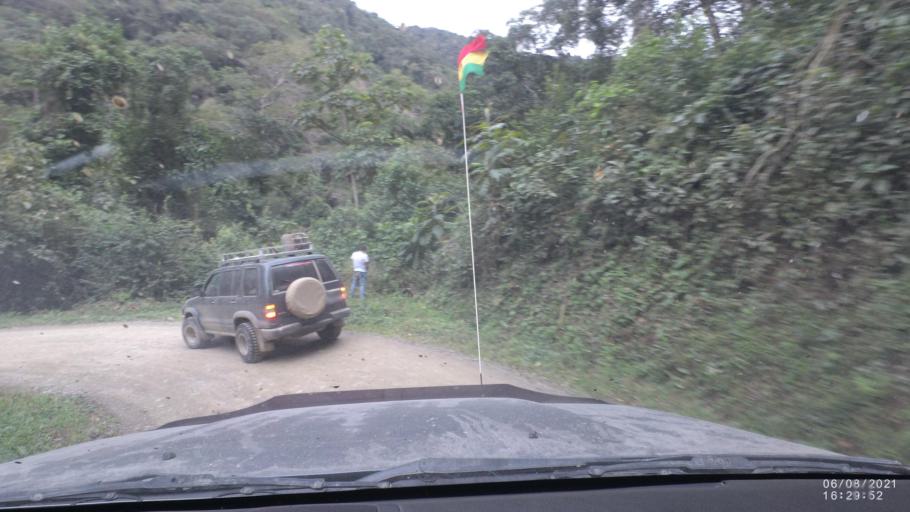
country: BO
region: La Paz
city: Quime
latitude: -16.5232
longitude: -66.7527
